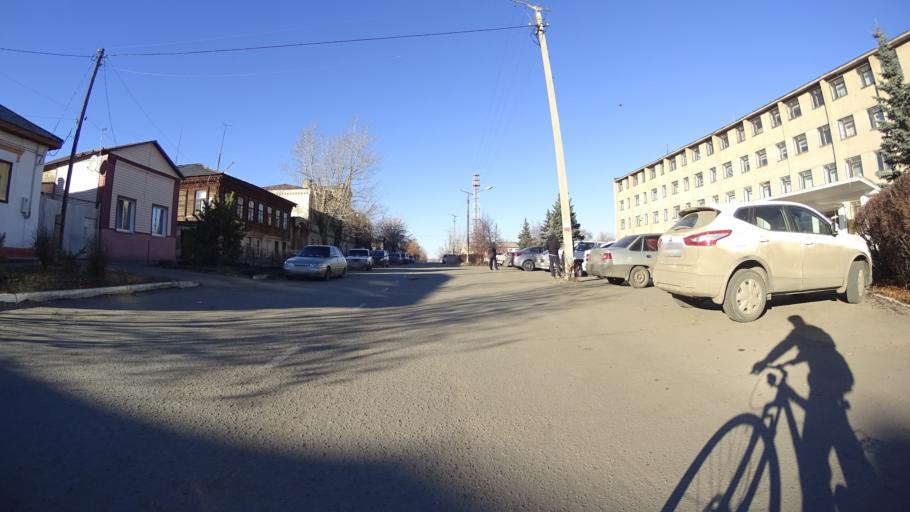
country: RU
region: Chelyabinsk
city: Troitsk
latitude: 54.0807
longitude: 61.5622
